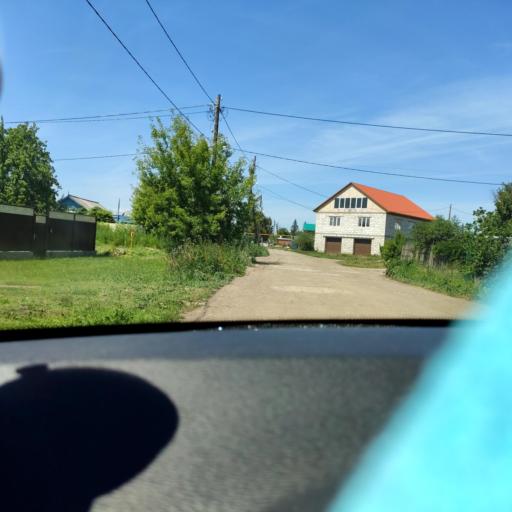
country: RU
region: Samara
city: Smyshlyayevka
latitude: 53.2427
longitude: 50.3534
